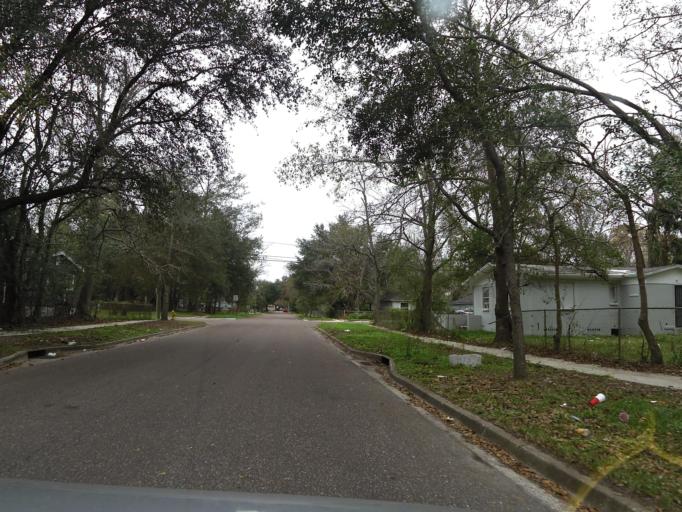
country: US
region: Florida
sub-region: Duval County
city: Jacksonville
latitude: 30.3736
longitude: -81.6935
